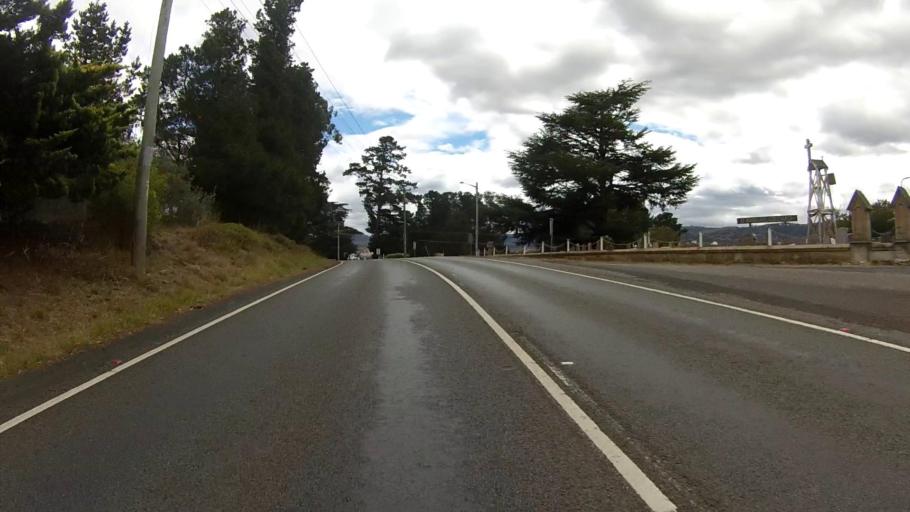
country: AU
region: Tasmania
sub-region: Brighton
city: Bridgewater
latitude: -42.6809
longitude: 147.2659
